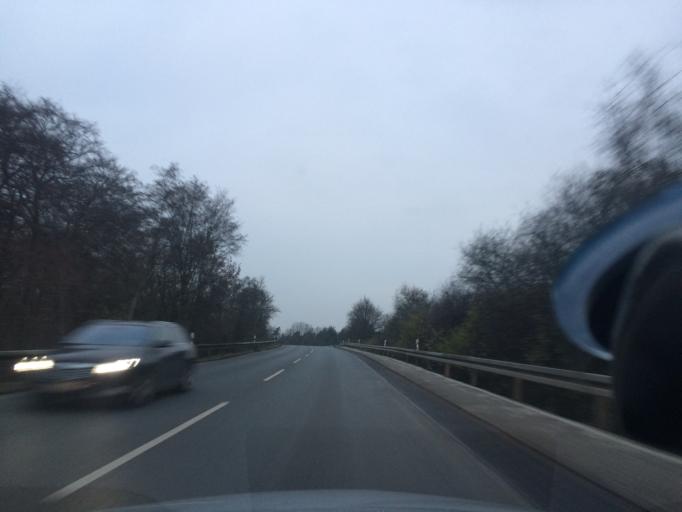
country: DE
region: Hesse
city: Morfelden-Walldorf
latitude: 50.0120
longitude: 8.5968
